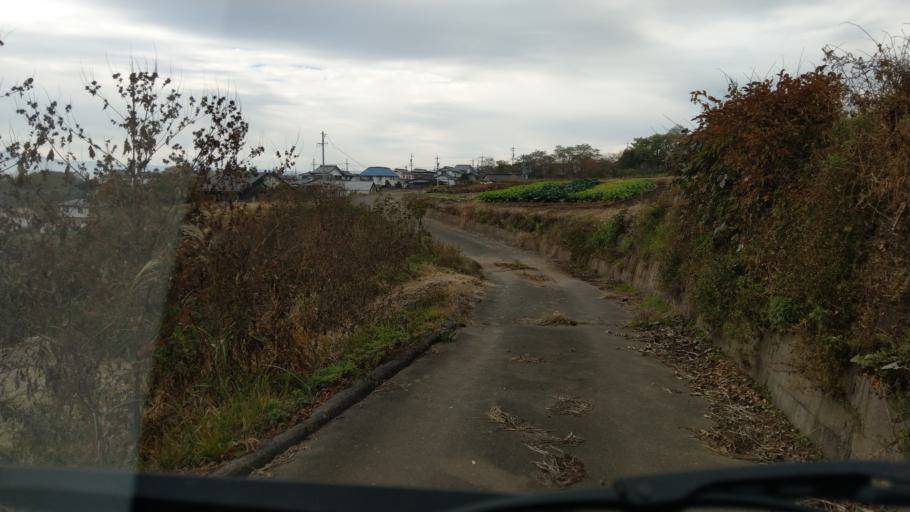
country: JP
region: Nagano
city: Komoro
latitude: 36.3171
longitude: 138.4588
